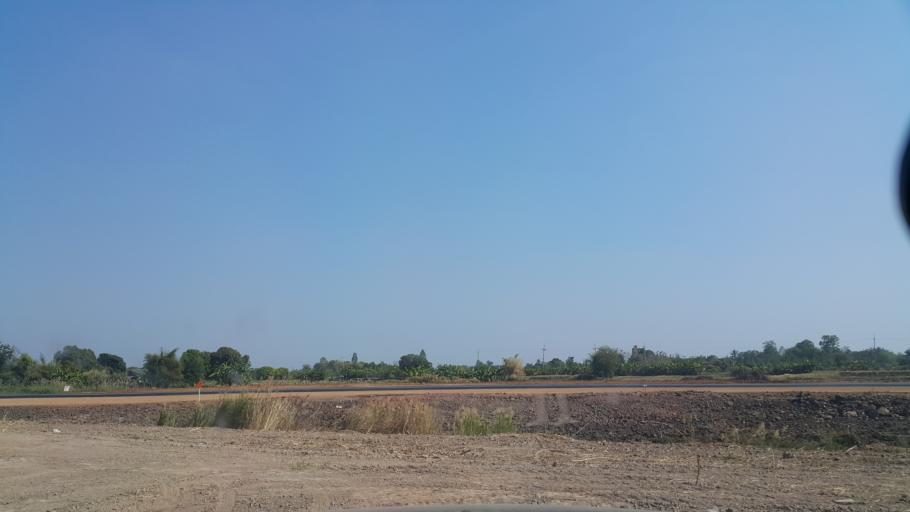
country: TH
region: Khon Kaen
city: Khon Kaen
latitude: 16.5095
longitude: 102.8716
